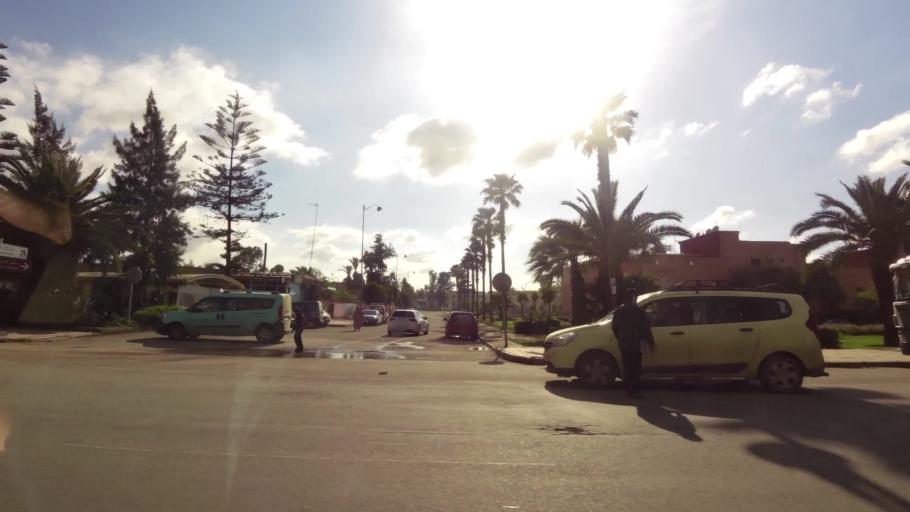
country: MA
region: Chaouia-Ouardigha
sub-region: Settat Province
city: Berrechid
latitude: 33.2634
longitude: -7.5824
